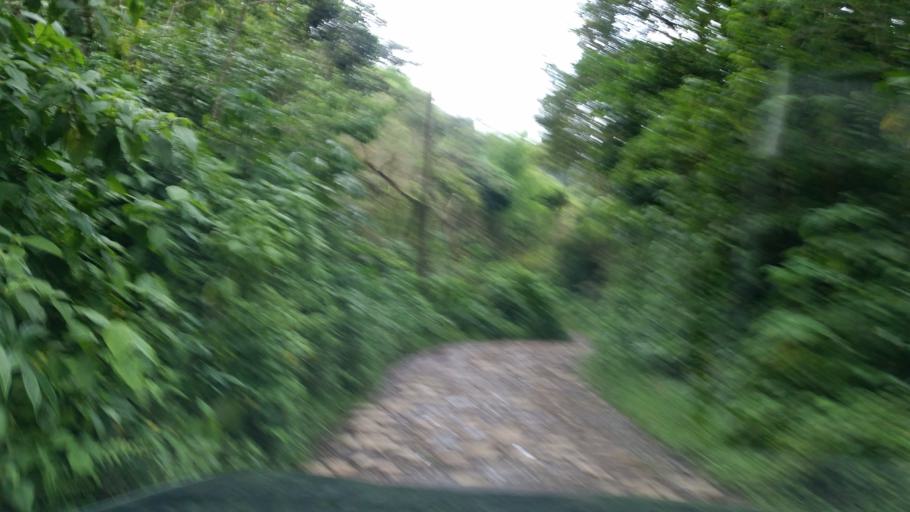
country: NI
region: Jinotega
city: San Jose de Bocay
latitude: 13.2738
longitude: -85.7171
